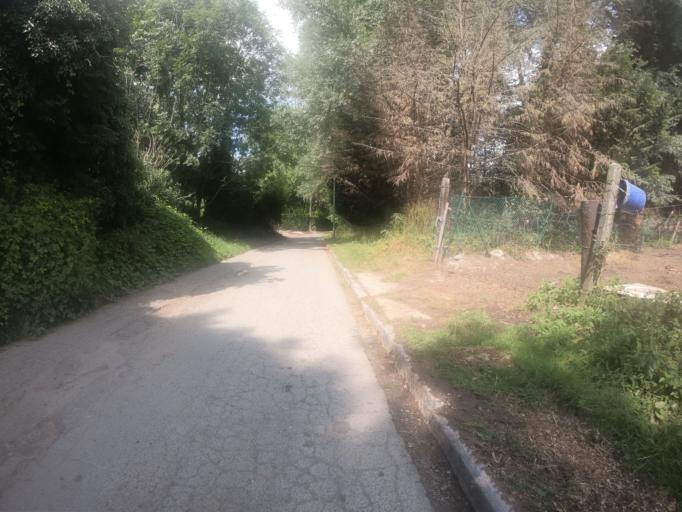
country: BE
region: Flanders
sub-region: Provincie Vlaams-Brabant
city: Dilbeek
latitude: 50.8294
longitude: 4.2740
